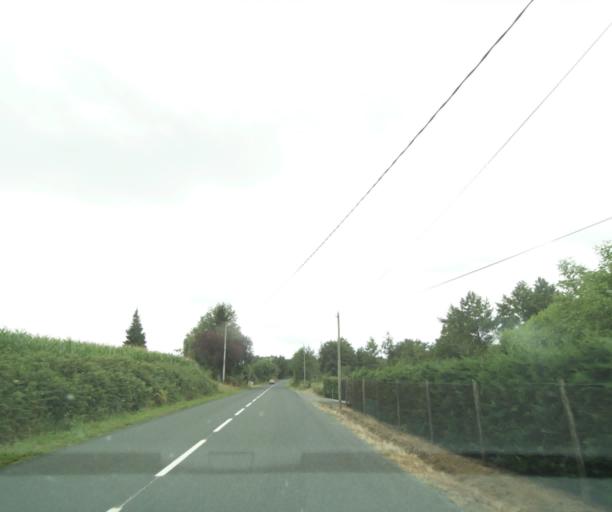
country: FR
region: Pays de la Loire
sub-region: Departement de Maine-et-Loire
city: Durtal
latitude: 47.7241
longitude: -0.2623
